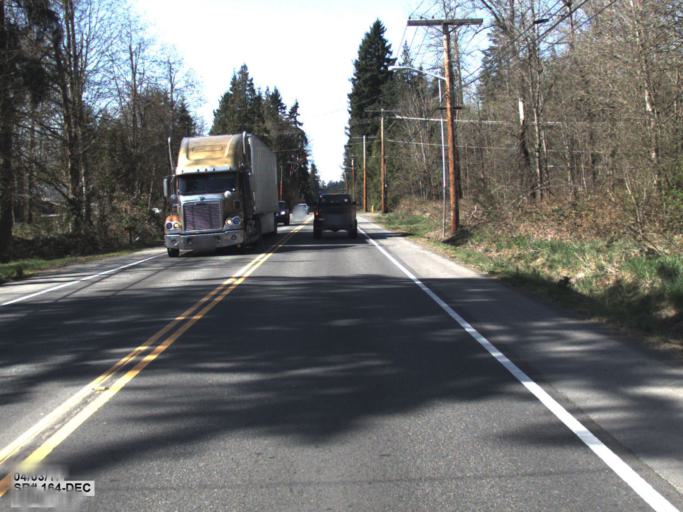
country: US
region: Washington
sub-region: King County
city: Lea Hill
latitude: 47.2821
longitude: -122.1684
